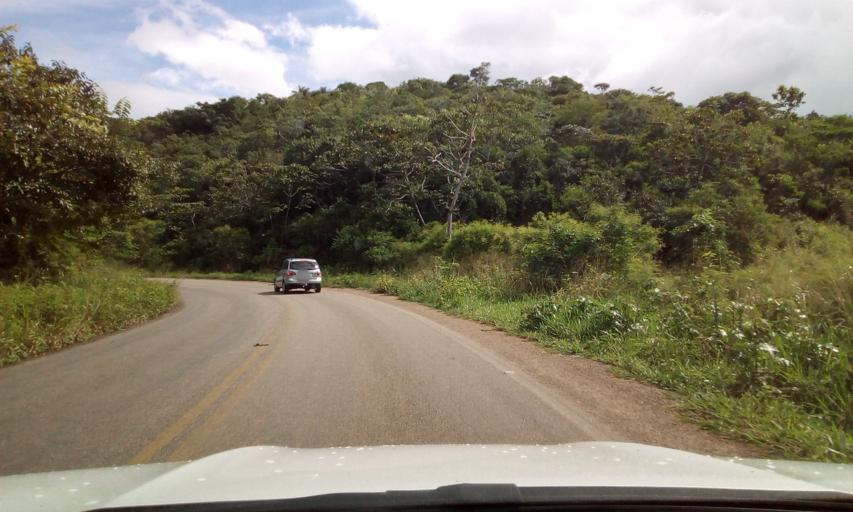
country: BR
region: Paraiba
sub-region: Areia
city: Areia
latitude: -6.9292
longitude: -35.6485
